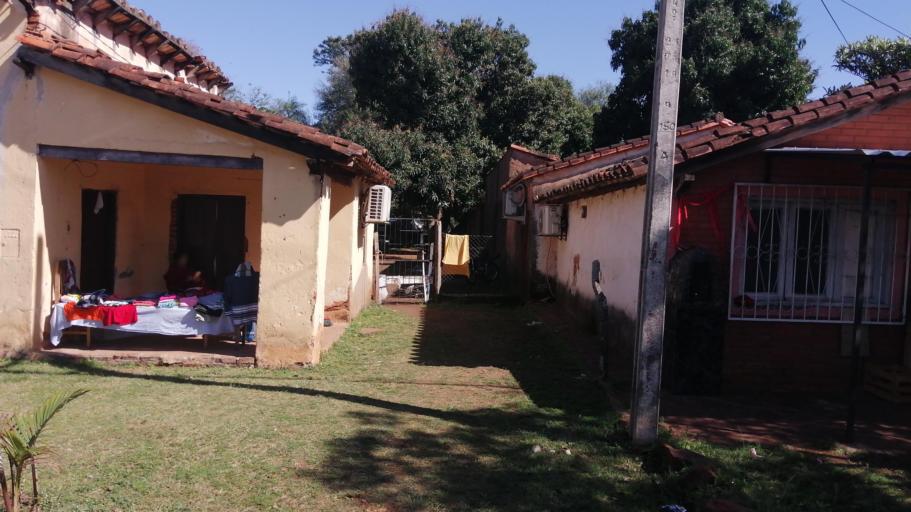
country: PY
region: Misiones
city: San Juan Bautista
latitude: -26.6731
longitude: -57.1420
